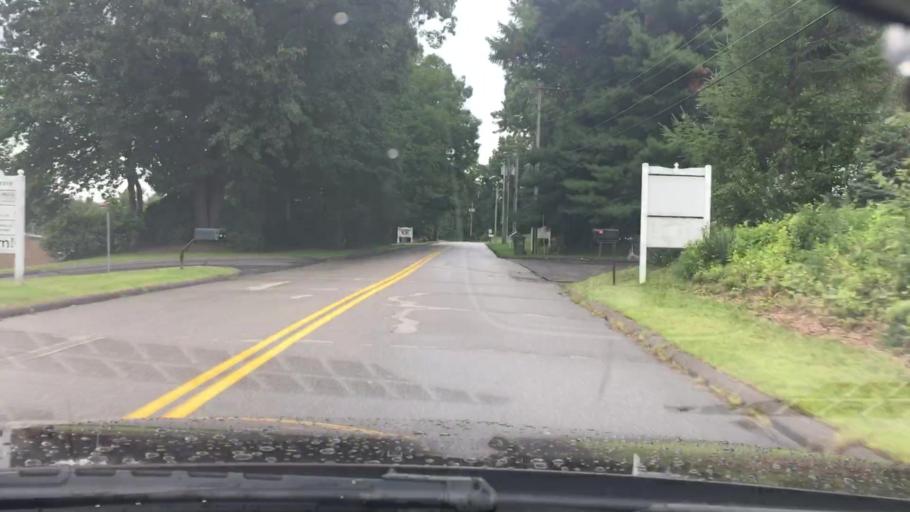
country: US
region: Connecticut
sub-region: Hartford County
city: Glastonbury Center
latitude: 41.7099
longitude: -72.5774
